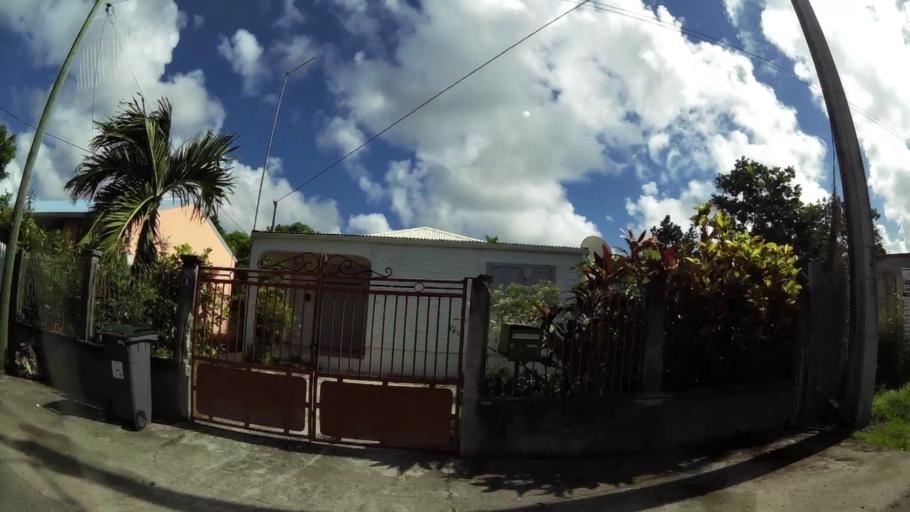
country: GP
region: Guadeloupe
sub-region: Guadeloupe
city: Port-Louis
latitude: 16.4199
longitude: -61.5288
